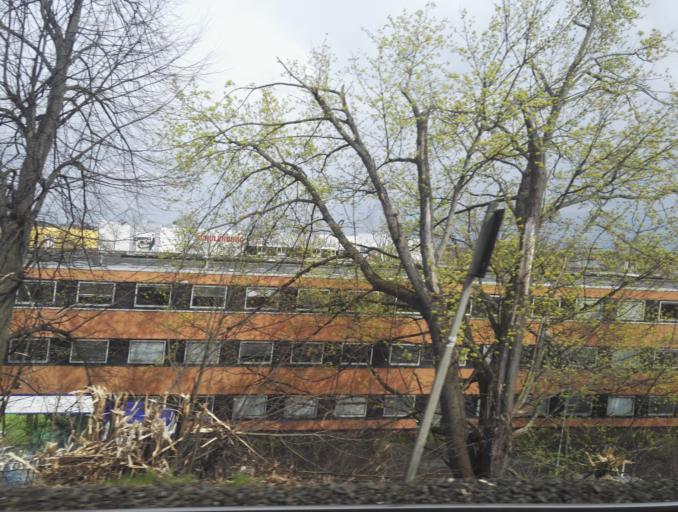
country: DE
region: Lower Saxony
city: Goslar
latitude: 51.9129
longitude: 10.4510
